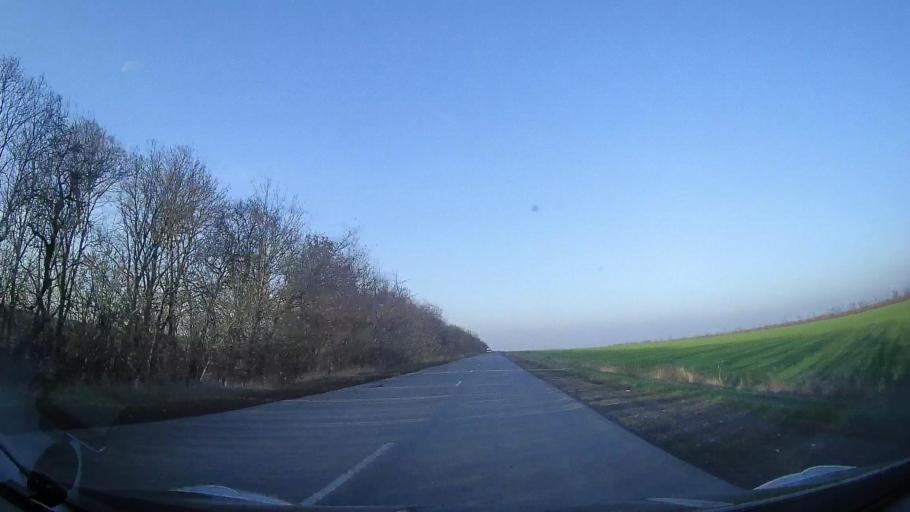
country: RU
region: Rostov
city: Kirovskaya
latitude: 47.0034
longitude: 39.9790
